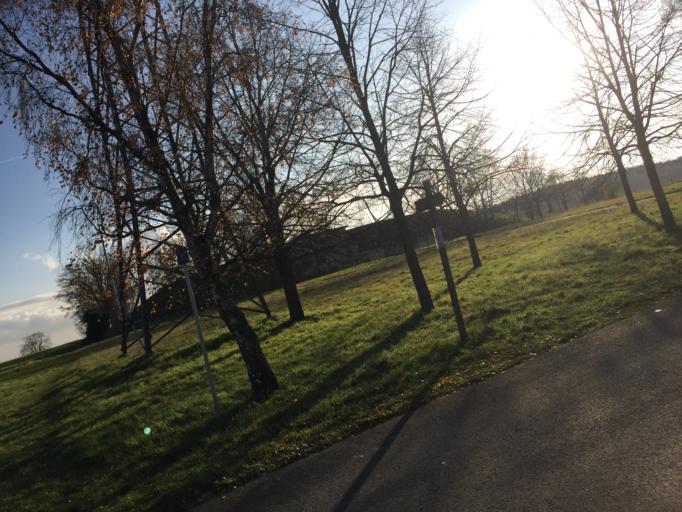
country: DE
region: Hesse
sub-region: Regierungsbezirk Giessen
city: Langgons
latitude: 50.5219
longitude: 8.7091
